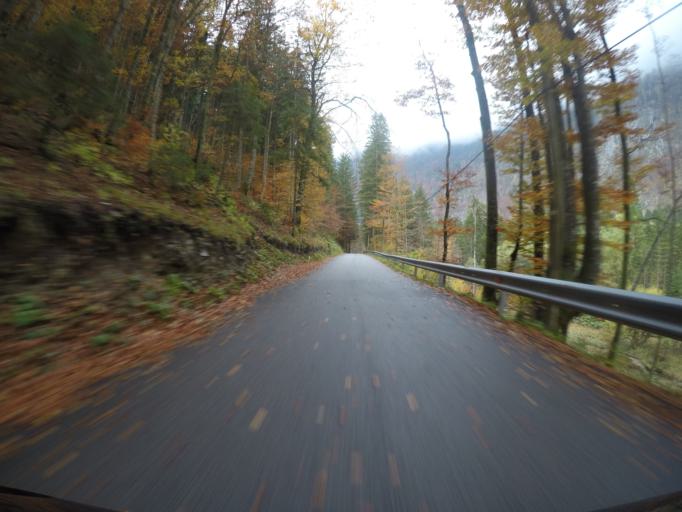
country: SI
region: Jesenice
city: Hrusica
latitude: 46.4000
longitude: 14.0010
